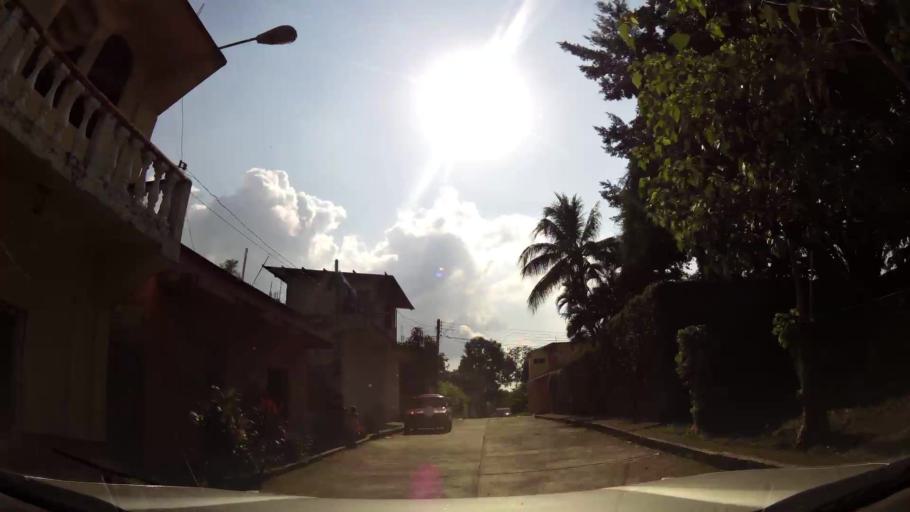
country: GT
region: Retalhuleu
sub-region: Municipio de Retalhuleu
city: Retalhuleu
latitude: 14.5395
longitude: -91.6837
